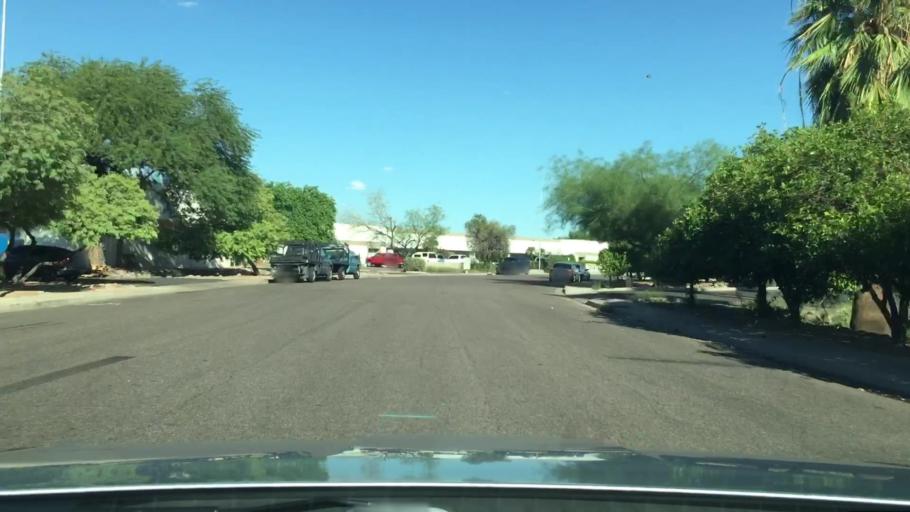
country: US
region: Arizona
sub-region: Maricopa County
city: Mesa
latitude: 33.3816
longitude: -111.8202
